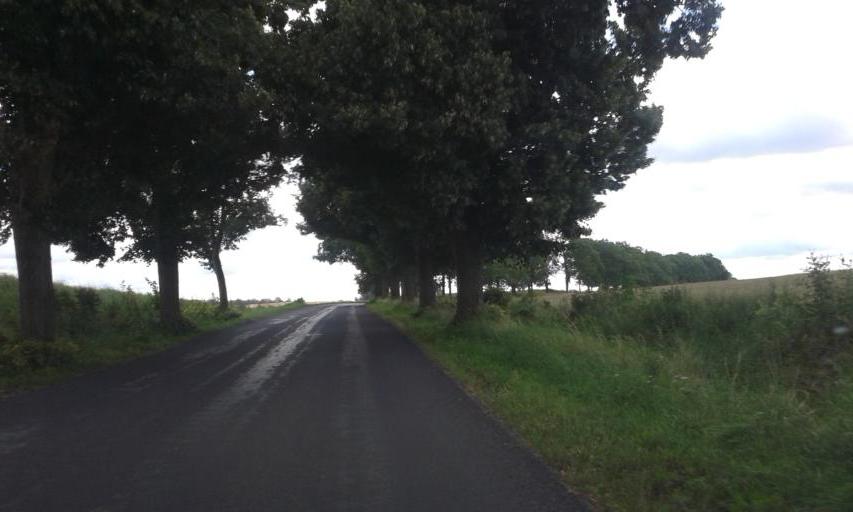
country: PL
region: West Pomeranian Voivodeship
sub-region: Powiat walecki
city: Walcz
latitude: 53.2293
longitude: 16.5422
